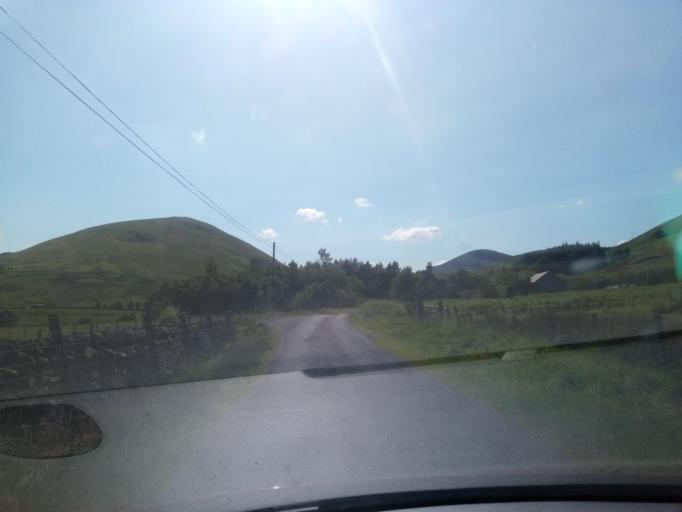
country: GB
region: Scotland
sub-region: The Scottish Borders
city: Peebles
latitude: 55.4960
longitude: -3.2367
